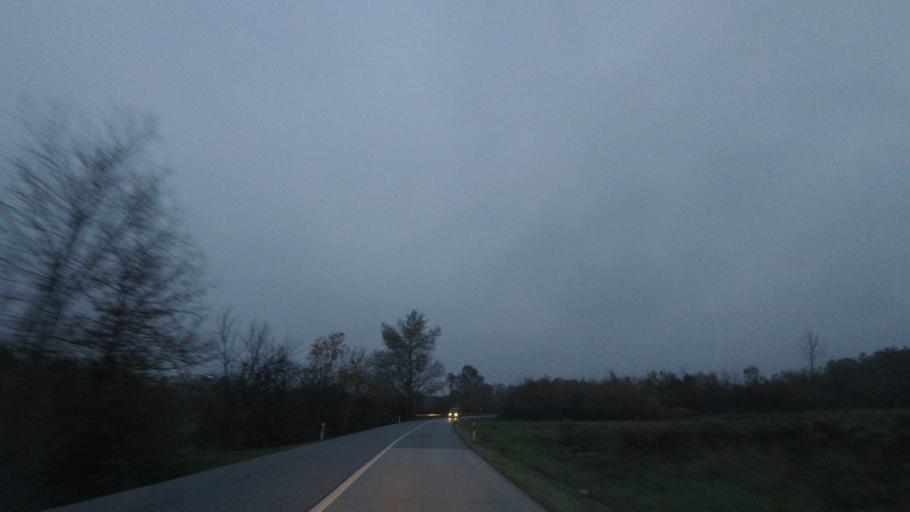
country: HR
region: Sisacko-Moslavacka
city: Glina
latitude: 45.3768
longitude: 16.1413
